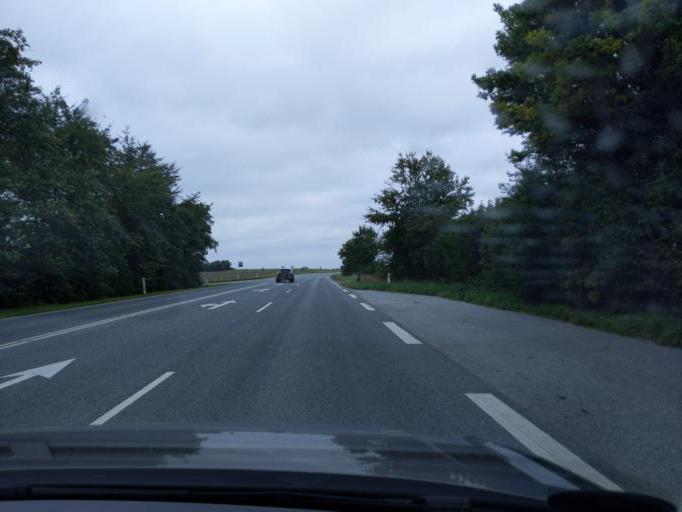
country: DK
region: North Denmark
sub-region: Mariagerfjord Kommune
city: Hobro
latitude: 56.5468
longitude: 9.8768
